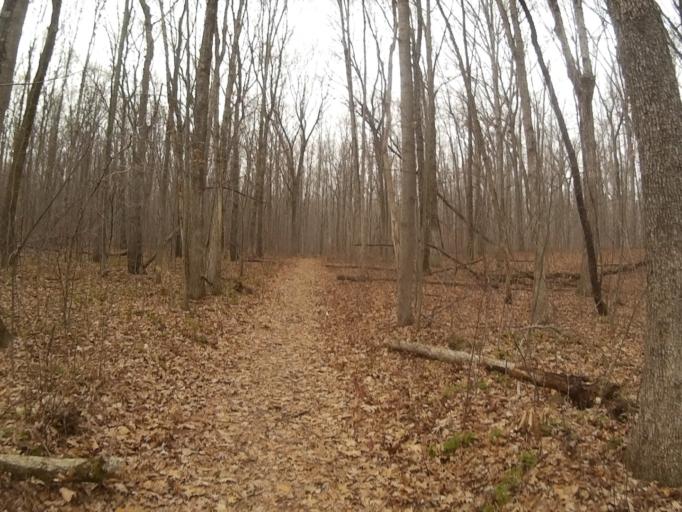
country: US
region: Pennsylvania
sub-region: Centre County
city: Park Forest Village
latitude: 40.7871
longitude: -77.9230
